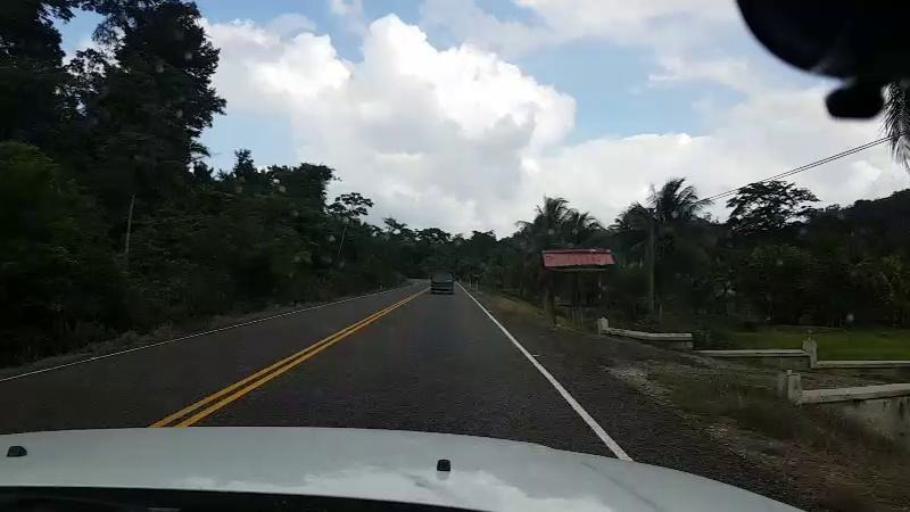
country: BZ
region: Cayo
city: Belmopan
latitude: 17.1513
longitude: -88.6674
